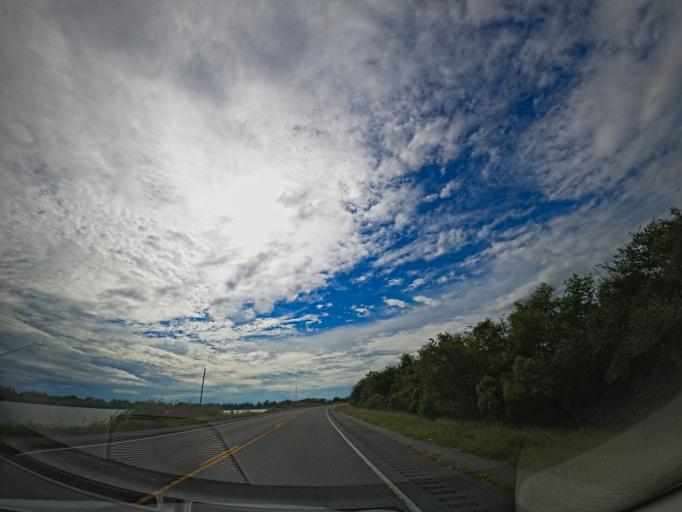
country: US
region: Louisiana
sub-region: Saint Tammany Parish
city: Eden Isle
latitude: 30.0908
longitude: -89.7736
